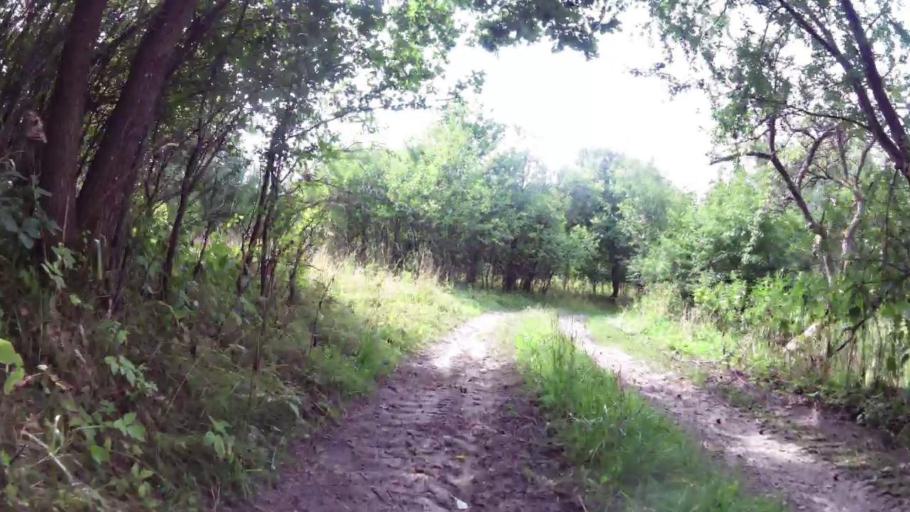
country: PL
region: West Pomeranian Voivodeship
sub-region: Powiat lobeski
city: Wegorzyno
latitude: 53.5273
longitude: 15.6188
